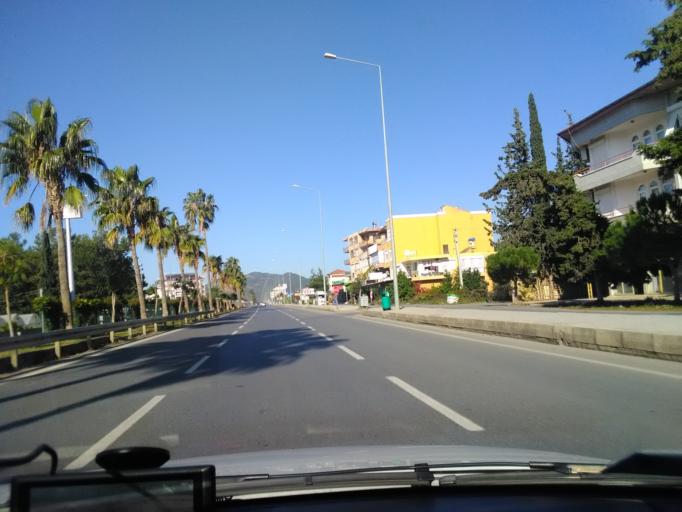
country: TR
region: Antalya
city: Gazipasa
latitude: 36.2794
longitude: 32.3037
